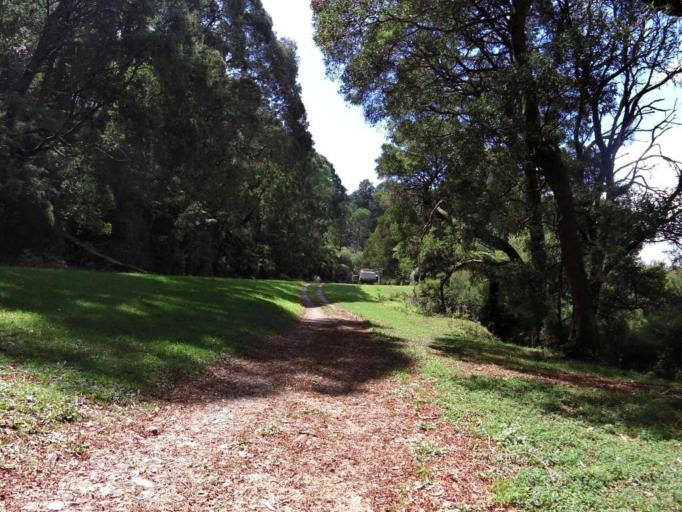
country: AU
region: Victoria
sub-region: Yarra Ranges
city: Millgrove
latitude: -37.7450
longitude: 145.6863
